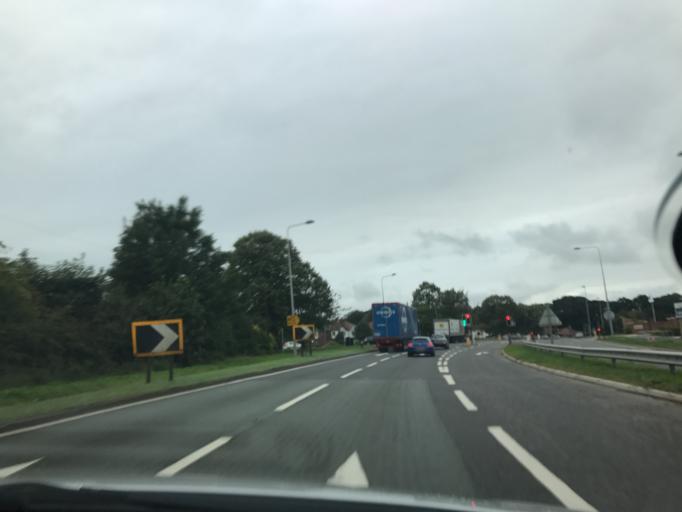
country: GB
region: England
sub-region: Cheshire West and Chester
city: Northwich
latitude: 53.2359
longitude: -2.5225
